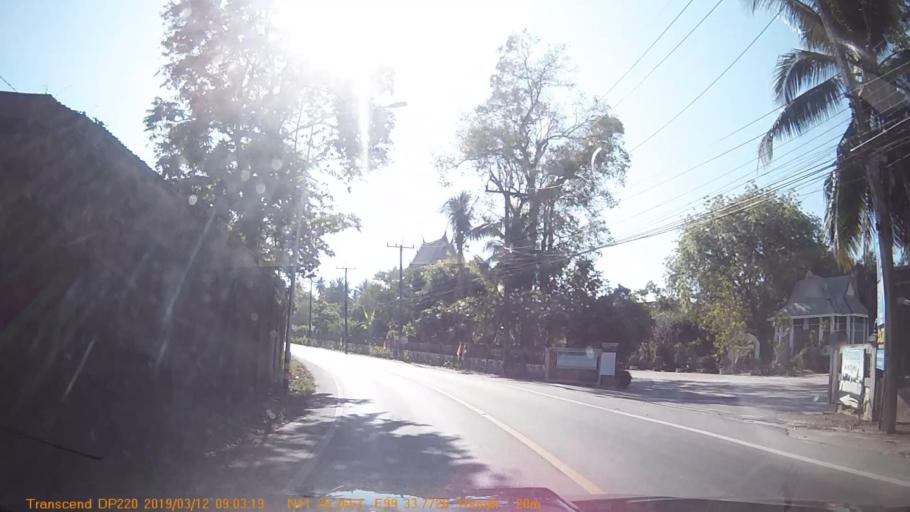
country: TH
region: Prachuap Khiri Khan
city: Thap Sakae
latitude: 11.4377
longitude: 99.5630
